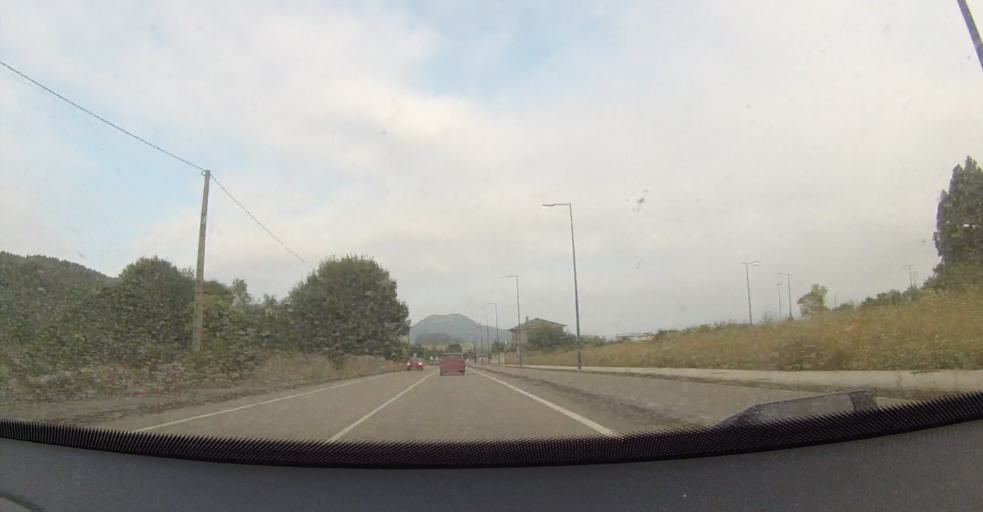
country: ES
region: Cantabria
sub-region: Provincia de Cantabria
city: Argonos
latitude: 43.4580
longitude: -3.5043
